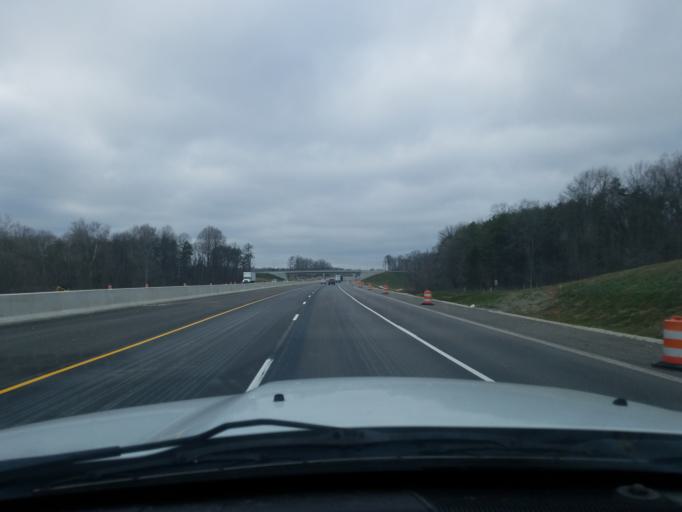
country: US
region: Indiana
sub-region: Monroe County
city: Bloomington
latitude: 39.1147
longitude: -86.5639
